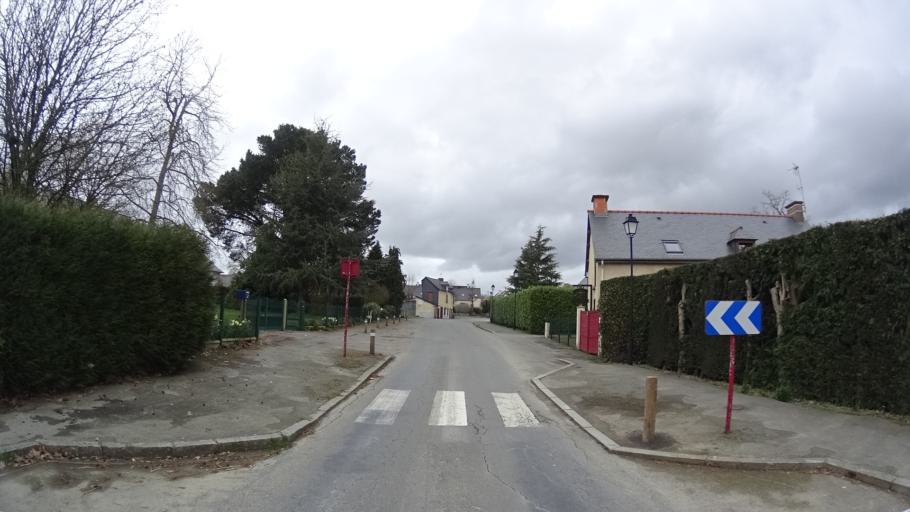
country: FR
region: Brittany
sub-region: Departement d'Ille-et-Vilaine
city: Saint-Gilles
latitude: 48.1910
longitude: -1.8321
